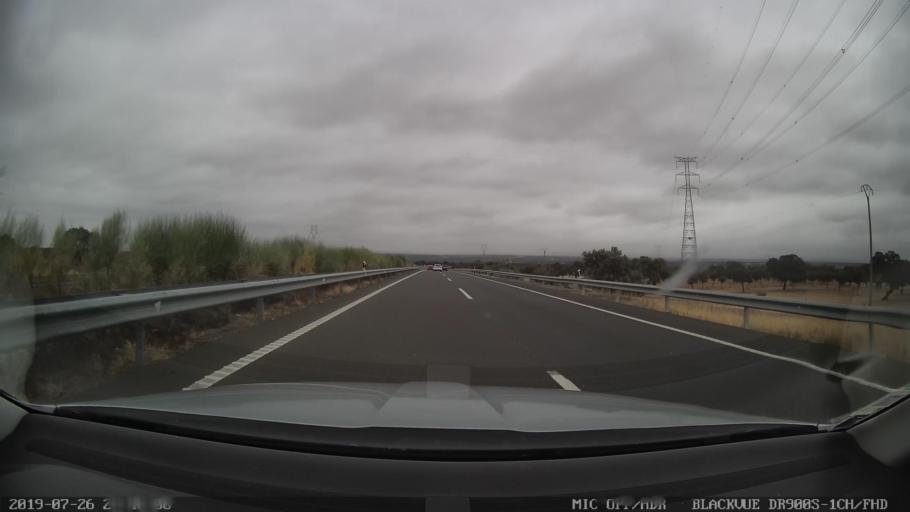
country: ES
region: Extremadura
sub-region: Provincia de Caceres
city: Jaraicejo
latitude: 39.5821
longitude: -5.8345
